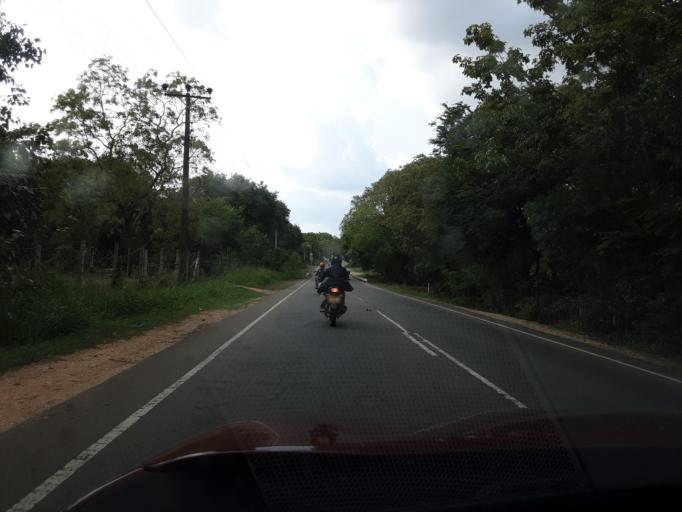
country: LK
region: Uva
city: Haputale
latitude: 6.5192
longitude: 81.1266
